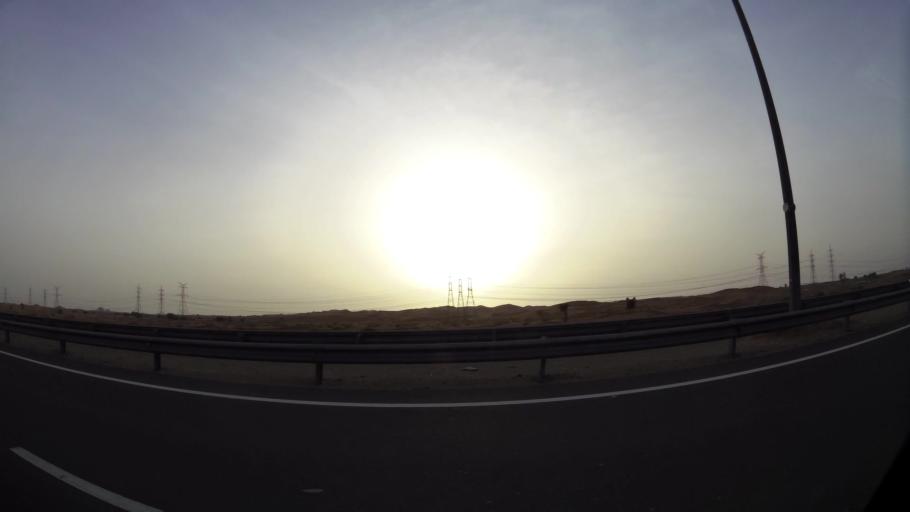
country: OM
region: Al Buraimi
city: Al Buraymi
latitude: 24.3085
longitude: 55.7463
